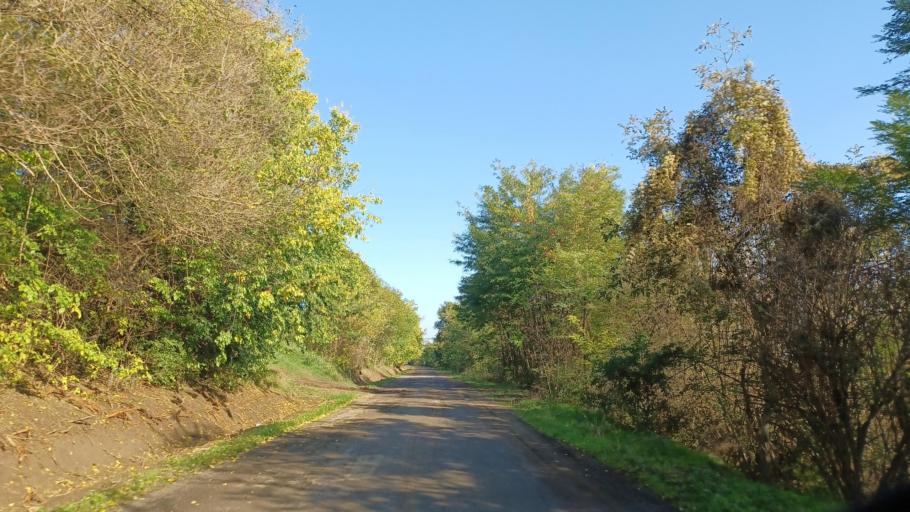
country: HU
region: Tolna
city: Szedres
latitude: 46.5250
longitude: 18.5923
